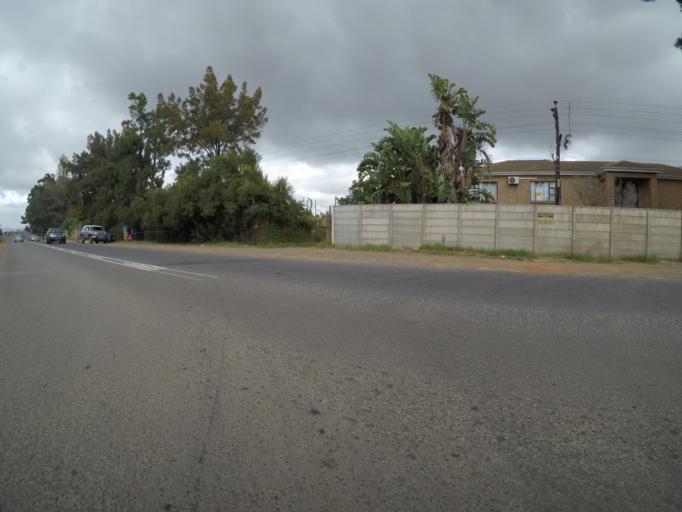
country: ZA
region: Western Cape
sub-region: City of Cape Town
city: Kraaifontein
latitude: -33.8322
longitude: 18.7355
